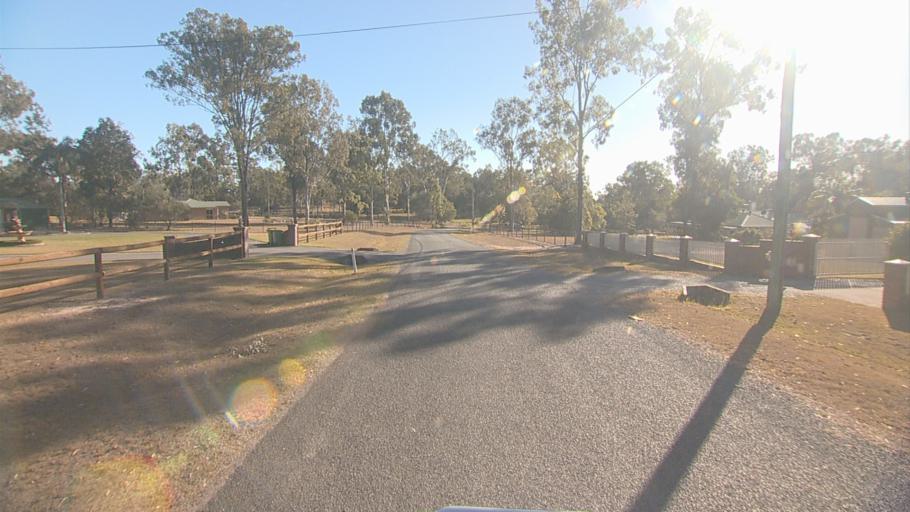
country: AU
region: Queensland
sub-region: Logan
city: Cedar Vale
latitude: -27.8414
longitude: 153.0107
